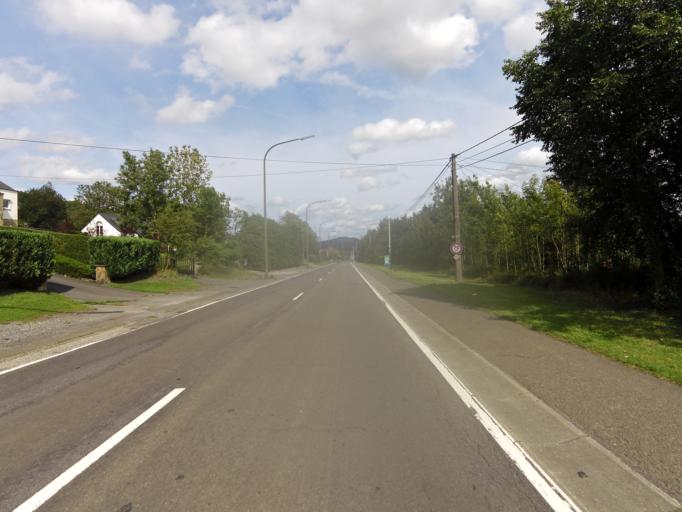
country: BE
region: Wallonia
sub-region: Province du Luxembourg
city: Durbuy
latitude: 50.3478
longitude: 5.4791
